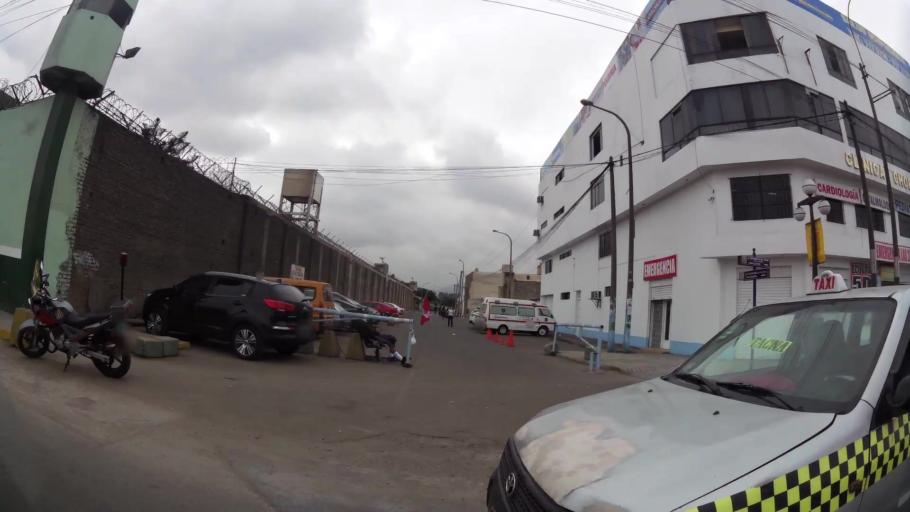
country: PE
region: Lima
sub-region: Lima
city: Surco
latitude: -12.1745
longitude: -77.0189
